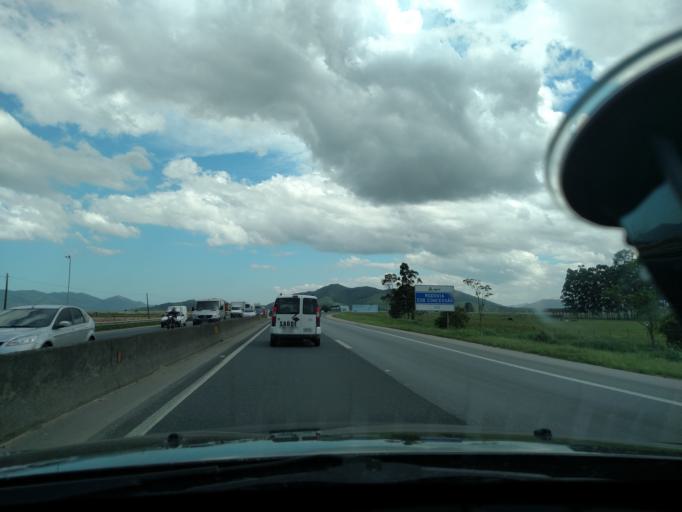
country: BR
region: Santa Catarina
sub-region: Tijucas
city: Tijucas
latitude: -27.2476
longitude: -48.6310
